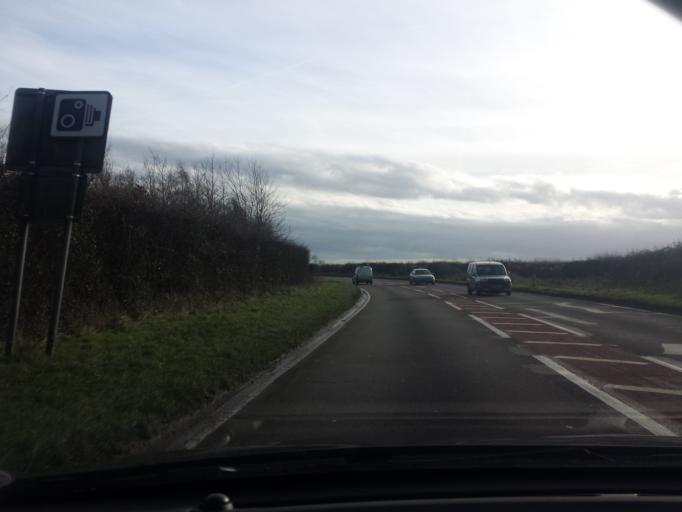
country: GB
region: England
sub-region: Essex
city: Great Bentley
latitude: 51.8670
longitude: 1.0763
